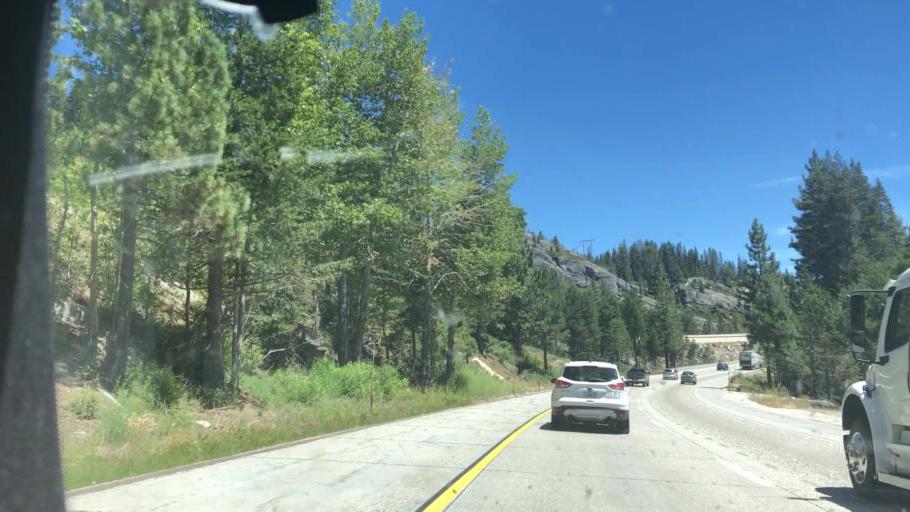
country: US
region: California
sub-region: Nevada County
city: Truckee
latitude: 39.3126
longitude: -120.5153
